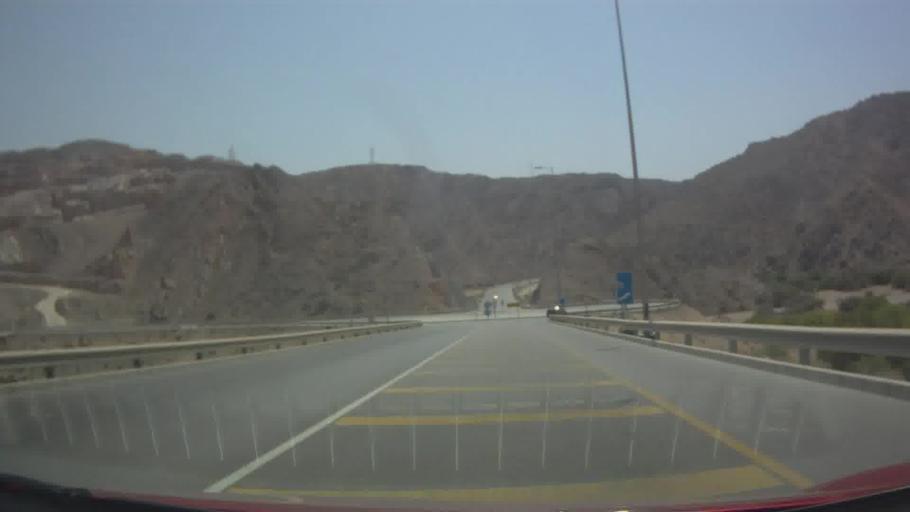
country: OM
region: Muhafazat Masqat
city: Muscat
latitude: 23.5357
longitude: 58.6494
